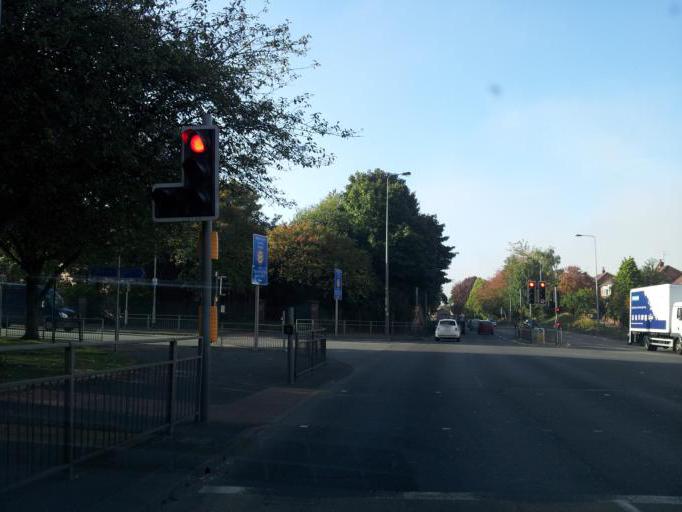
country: GB
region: England
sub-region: Borough of Oldham
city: Oldham
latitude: 53.5445
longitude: -2.1471
